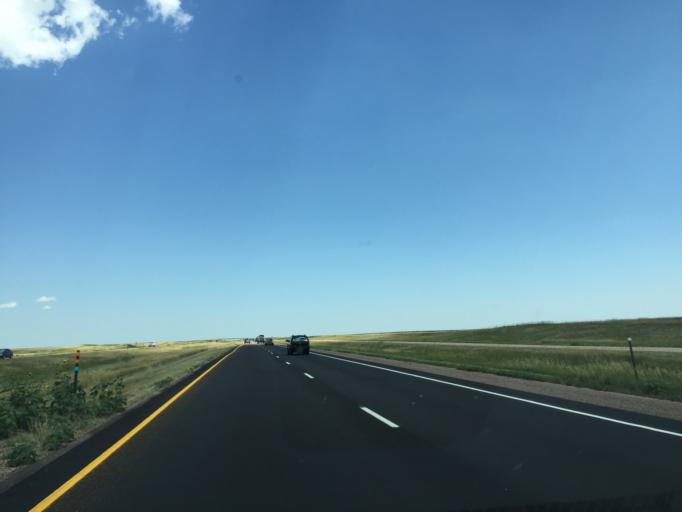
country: US
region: Colorado
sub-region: Lincoln County
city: Hugo
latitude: 39.2799
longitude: -103.3731
